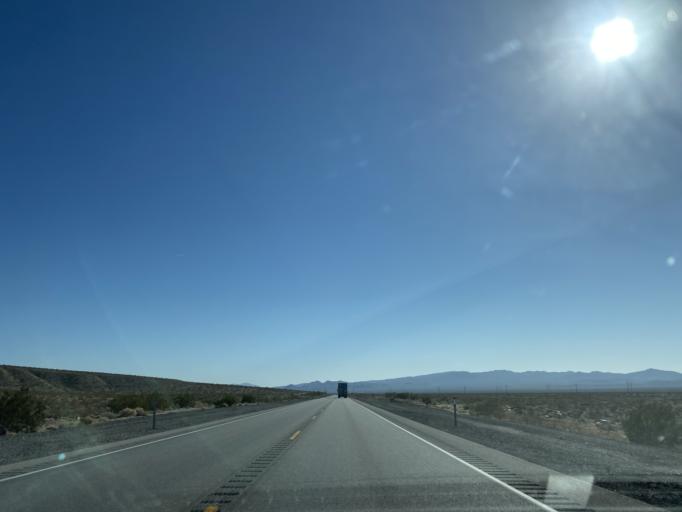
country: US
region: Nevada
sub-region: Nye County
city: Beatty
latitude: 36.8652
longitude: -116.7563
